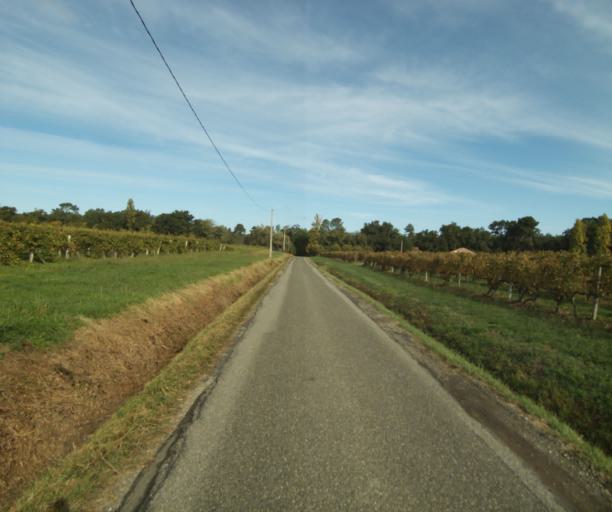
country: FR
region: Midi-Pyrenees
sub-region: Departement du Gers
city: Eauze
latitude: 43.9102
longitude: 0.1411
